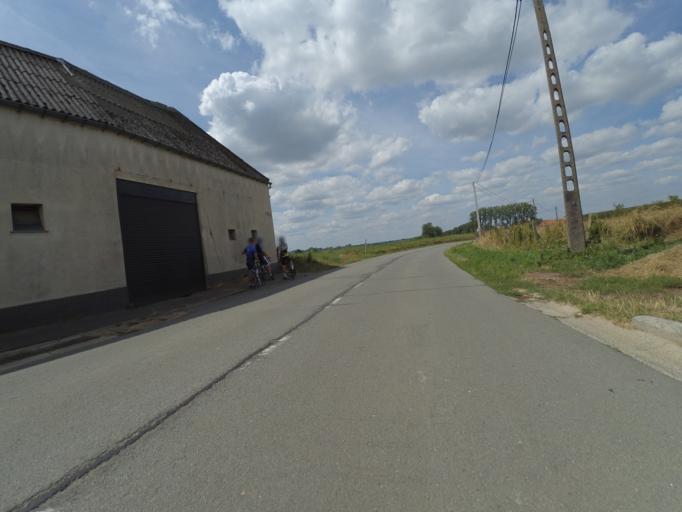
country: BE
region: Flanders
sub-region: Provincie Oost-Vlaanderen
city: Zottegem
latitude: 50.8337
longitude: 3.7314
